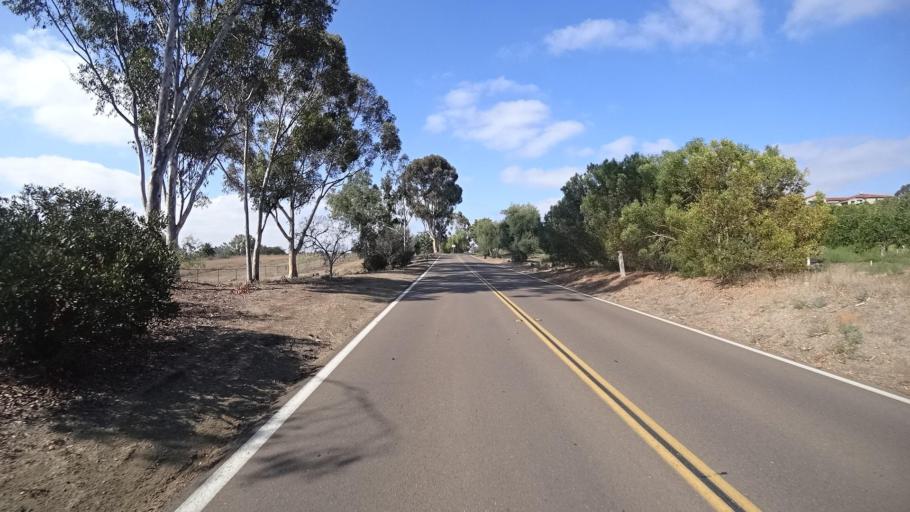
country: US
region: California
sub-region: San Diego County
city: Rancho Santa Fe
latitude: 33.0427
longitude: -117.1929
